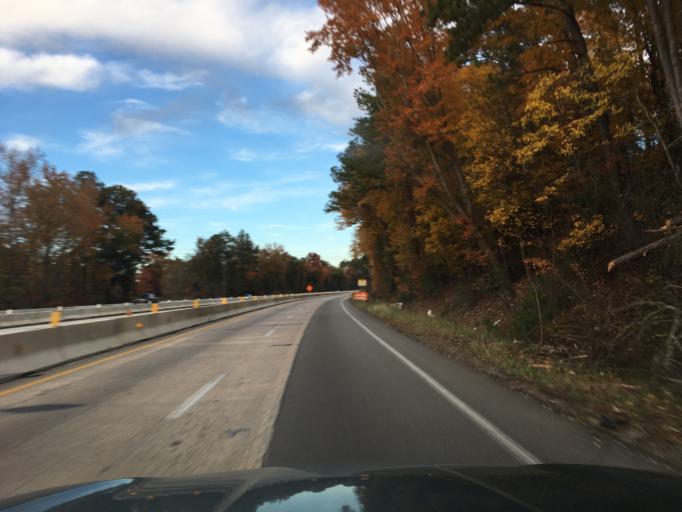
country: US
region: South Carolina
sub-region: Lexington County
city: Oak Grove
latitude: 34.0005
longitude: -81.1726
